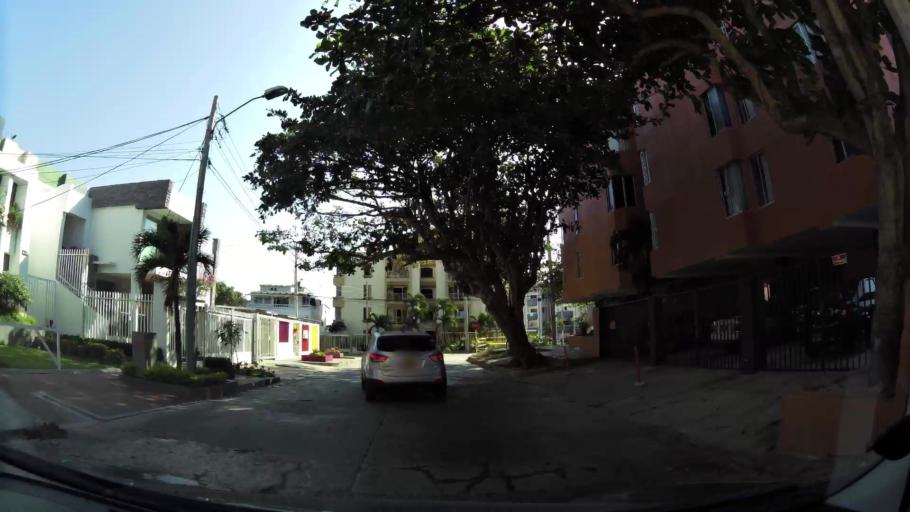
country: CO
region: Atlantico
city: Barranquilla
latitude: 11.0006
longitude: -74.8319
